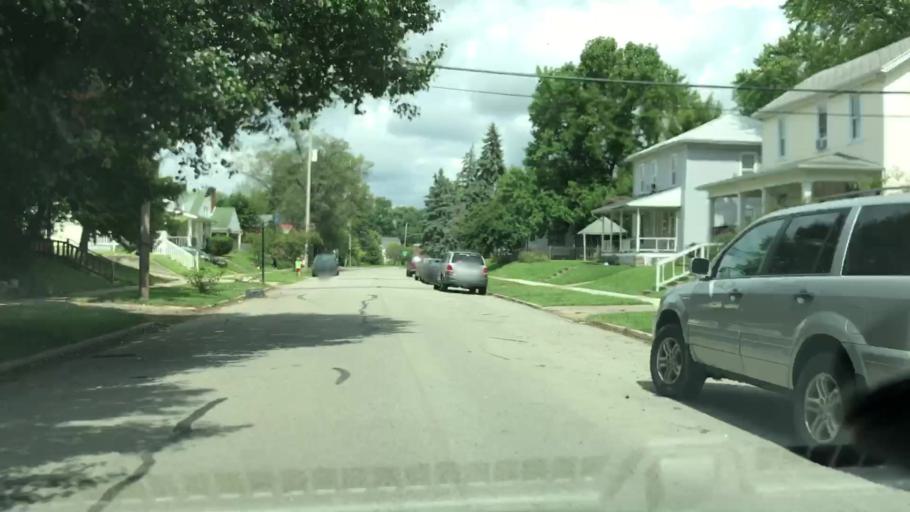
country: US
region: Ohio
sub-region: Greene County
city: Fairborn
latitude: 39.8216
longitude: -84.0166
